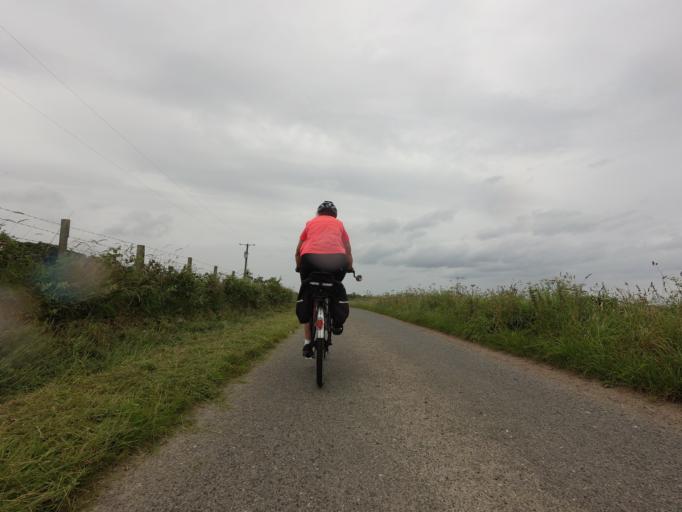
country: GB
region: Scotland
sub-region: Moray
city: Cullen
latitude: 57.6693
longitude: -2.7688
